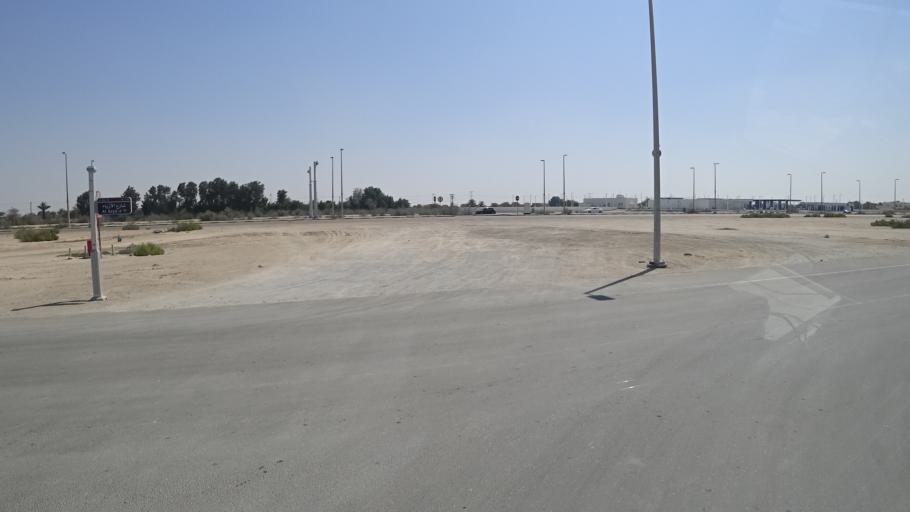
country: AE
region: Abu Dhabi
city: Abu Dhabi
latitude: 24.5446
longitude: 54.6358
